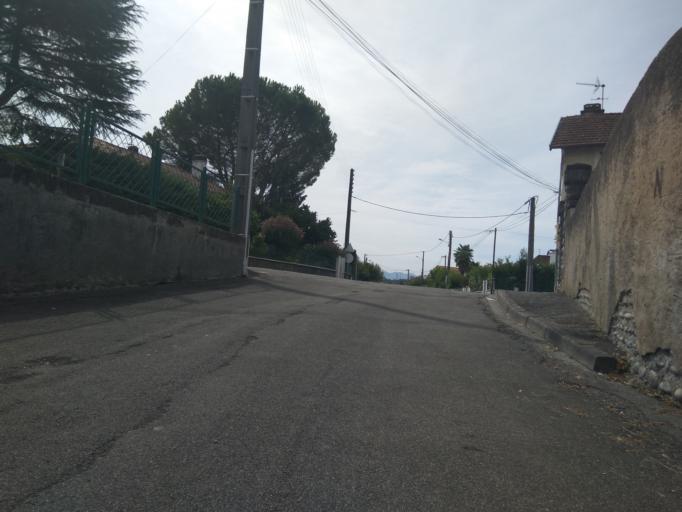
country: FR
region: Aquitaine
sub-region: Departement des Pyrenees-Atlantiques
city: Bizanos
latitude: 43.2928
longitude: -0.3474
